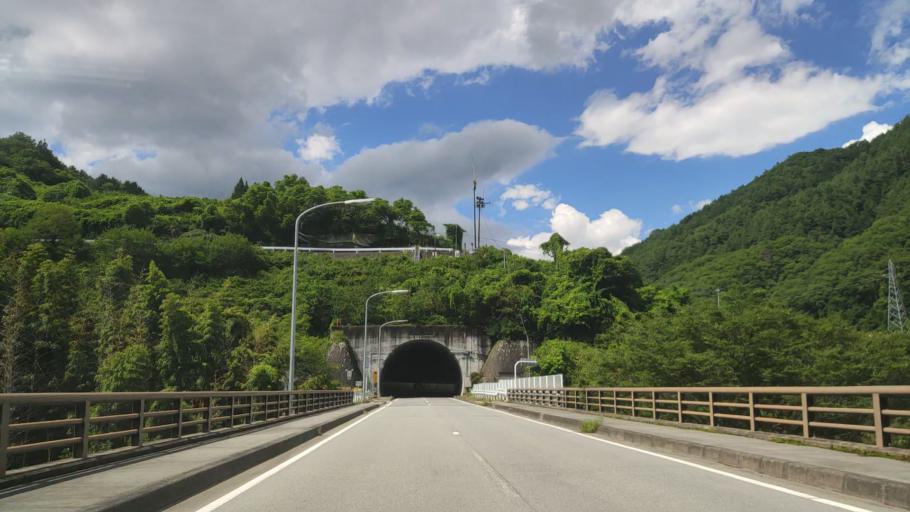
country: JP
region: Yamanashi
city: Enzan
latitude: 35.7784
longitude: 138.7386
